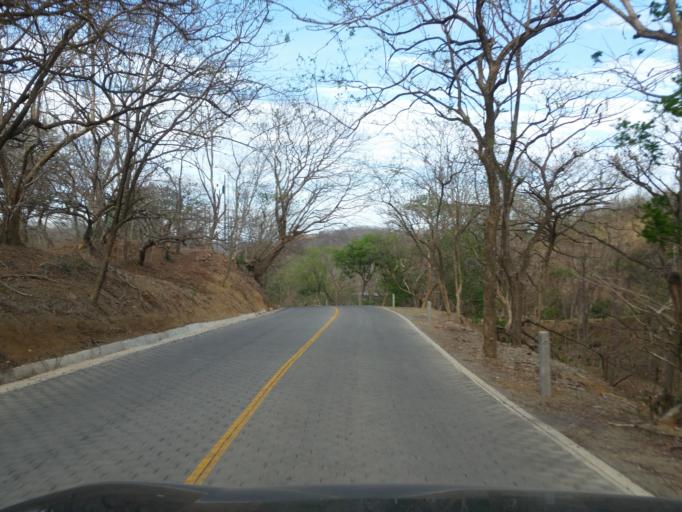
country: NI
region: Rivas
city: Tola
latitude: 11.3911
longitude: -85.9830
